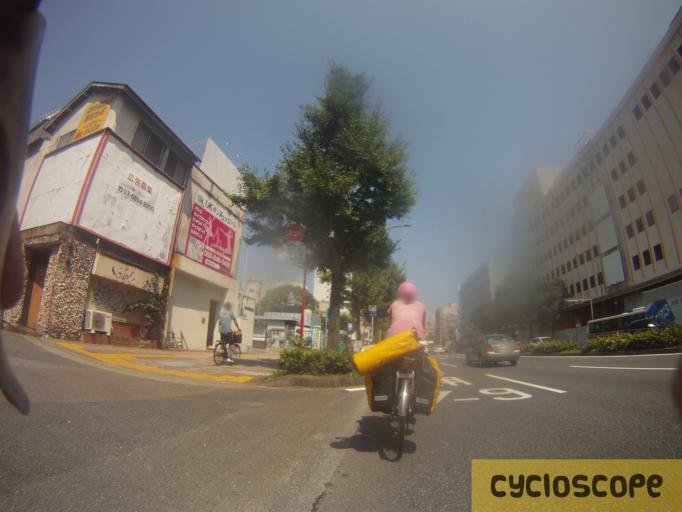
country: JP
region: Fukuoka
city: Fukuoka-shi
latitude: 33.5860
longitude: 130.3635
